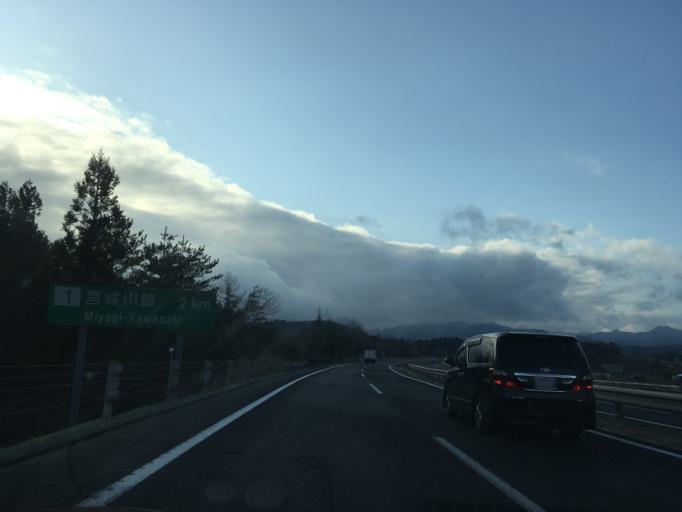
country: JP
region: Miyagi
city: Okawara
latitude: 38.1658
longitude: 140.6424
